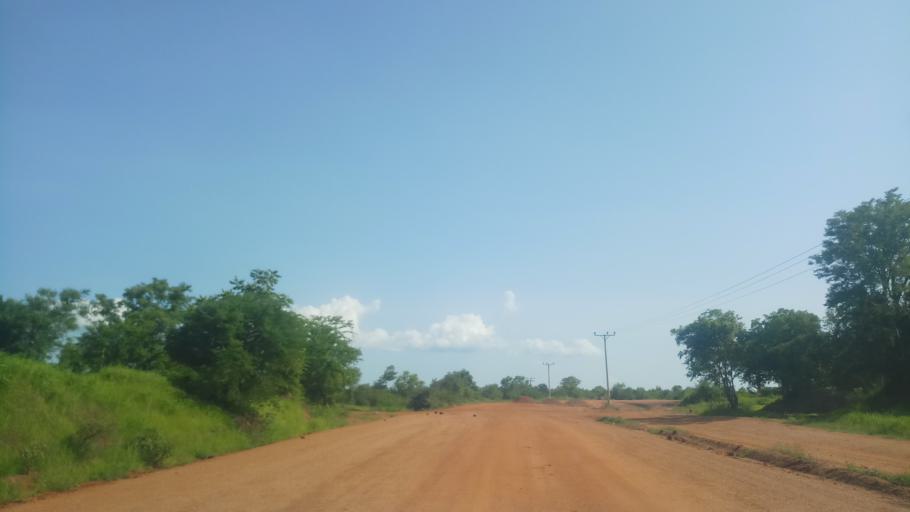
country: ET
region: Gambela
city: Gambela
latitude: 8.1344
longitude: 34.2969
